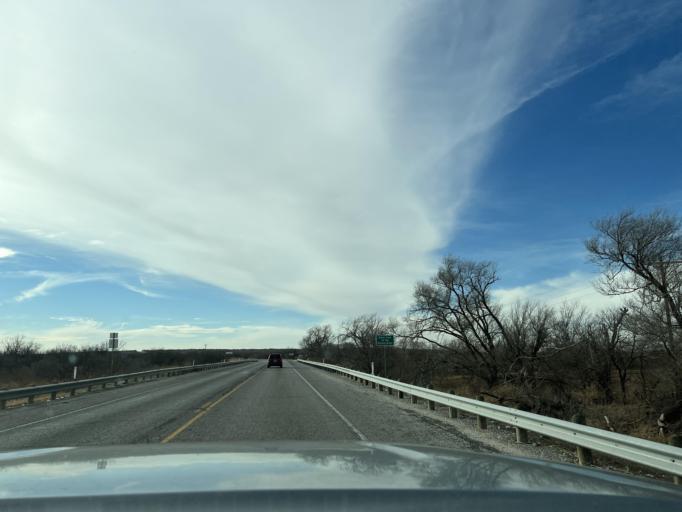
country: US
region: Texas
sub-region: Fisher County
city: Roby
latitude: 32.7612
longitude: -100.3066
